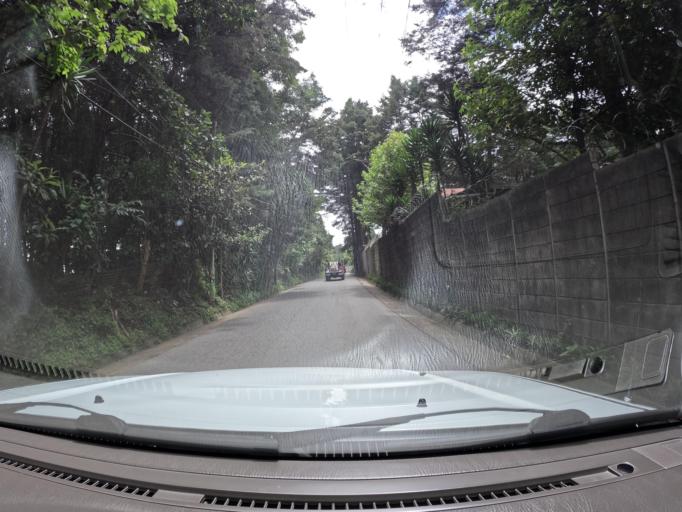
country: GT
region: Guatemala
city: Villa Canales
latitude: 14.4762
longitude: -90.4897
